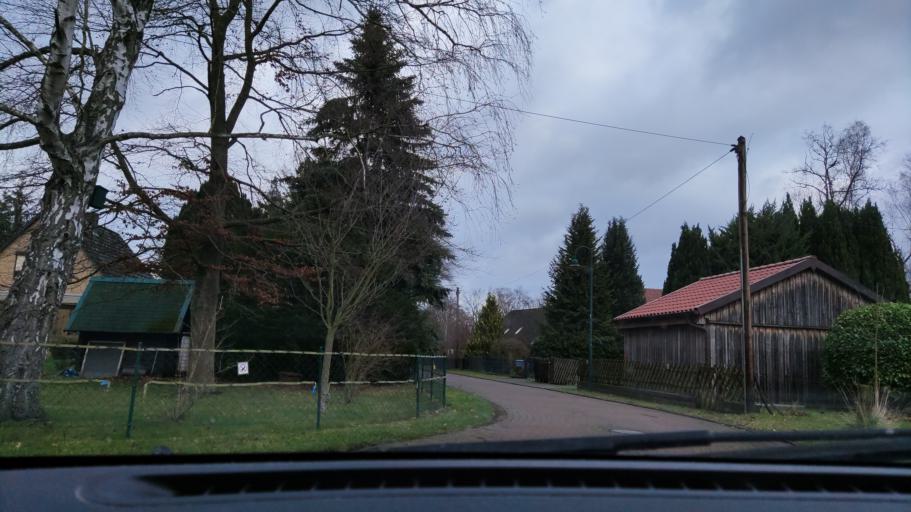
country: DE
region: Lower Saxony
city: Bienenbuttel
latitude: 53.1298
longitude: 10.4809
